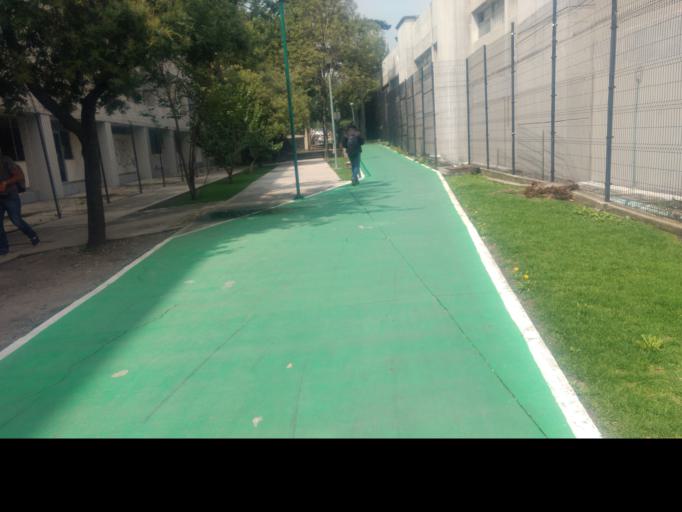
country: MX
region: Mexico City
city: Coyoacan
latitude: 19.3250
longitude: -99.1800
